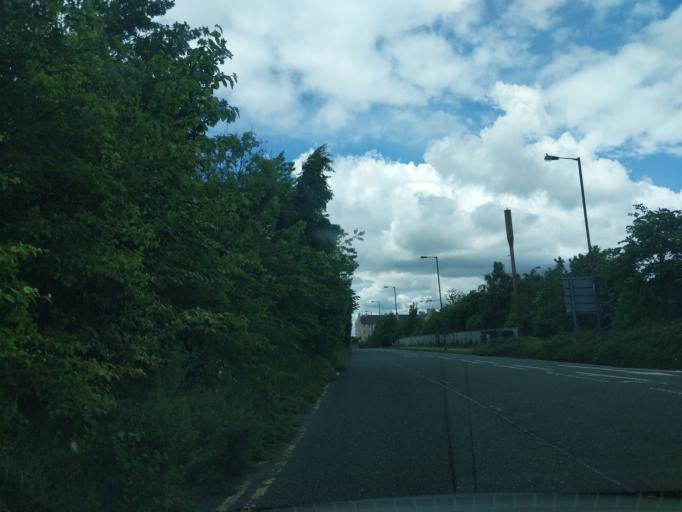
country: GB
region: Scotland
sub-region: Edinburgh
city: Edinburgh
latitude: 55.9690
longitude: -3.2396
